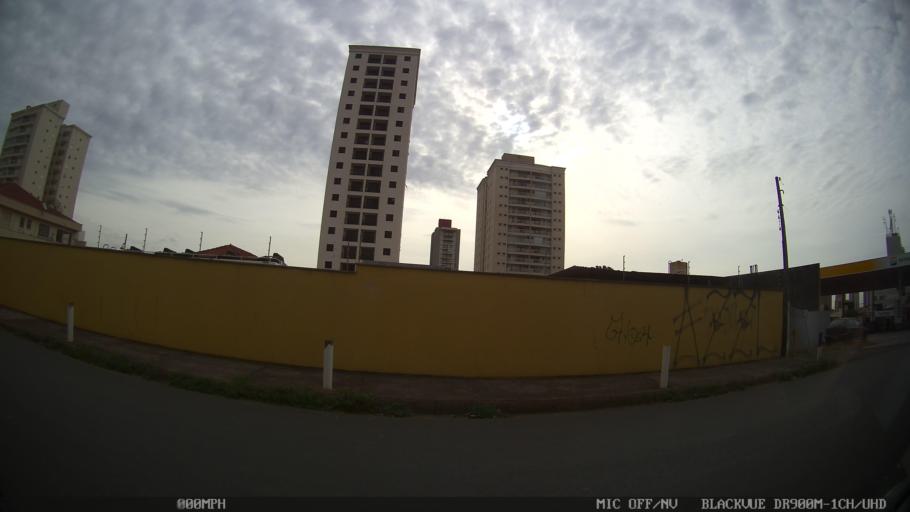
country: BR
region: Sao Paulo
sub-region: Piracicaba
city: Piracicaba
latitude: -22.7237
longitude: -47.6358
